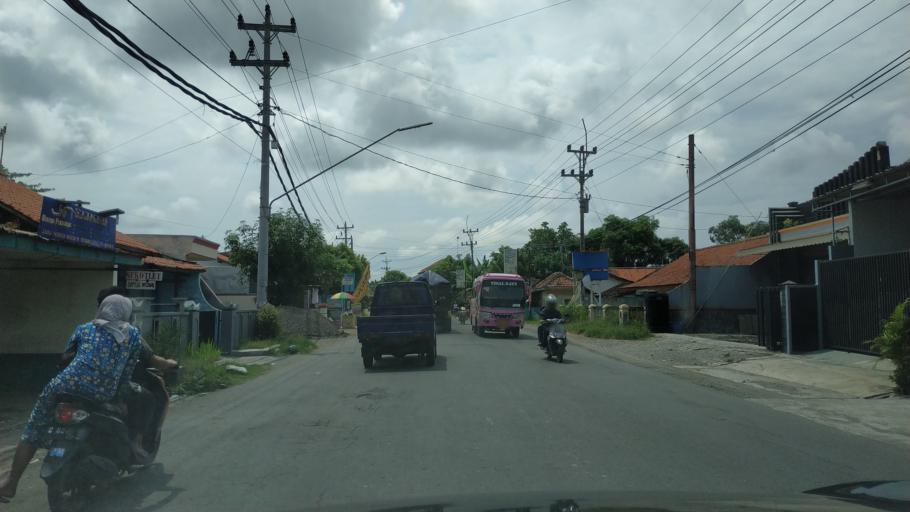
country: ID
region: Central Java
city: Adiwerna
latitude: -6.9062
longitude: 109.1265
